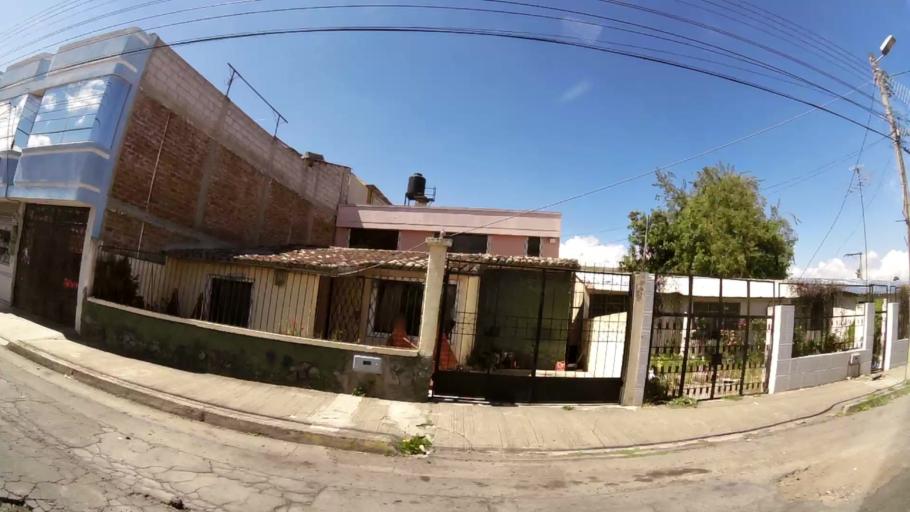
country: EC
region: Chimborazo
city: Riobamba
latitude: -1.6719
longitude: -78.6390
